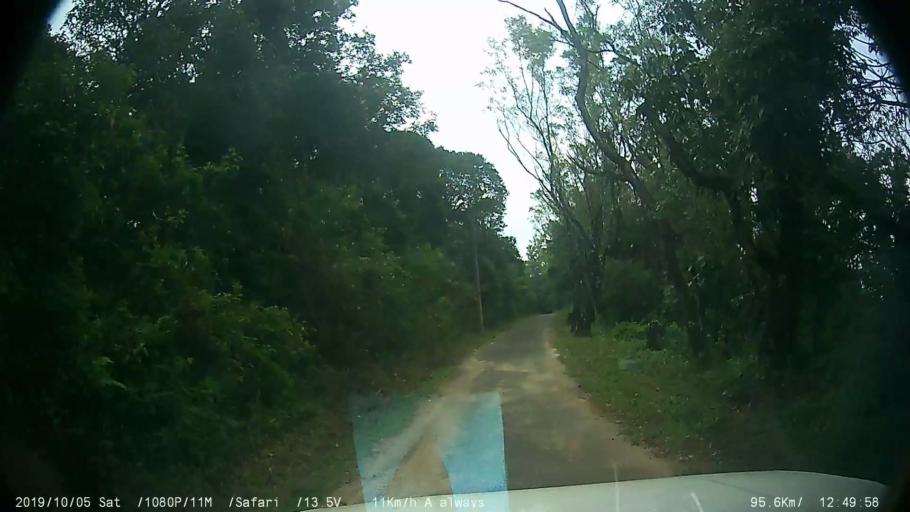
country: IN
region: Kerala
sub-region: Kottayam
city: Erattupetta
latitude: 9.5747
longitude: 76.9701
